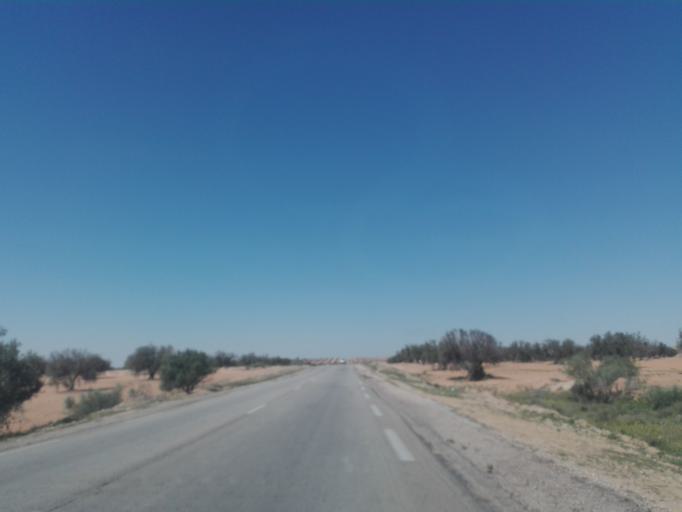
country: TN
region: Safaqis
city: Bi'r `Ali Bin Khalifah
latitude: 34.7587
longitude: 10.2980
